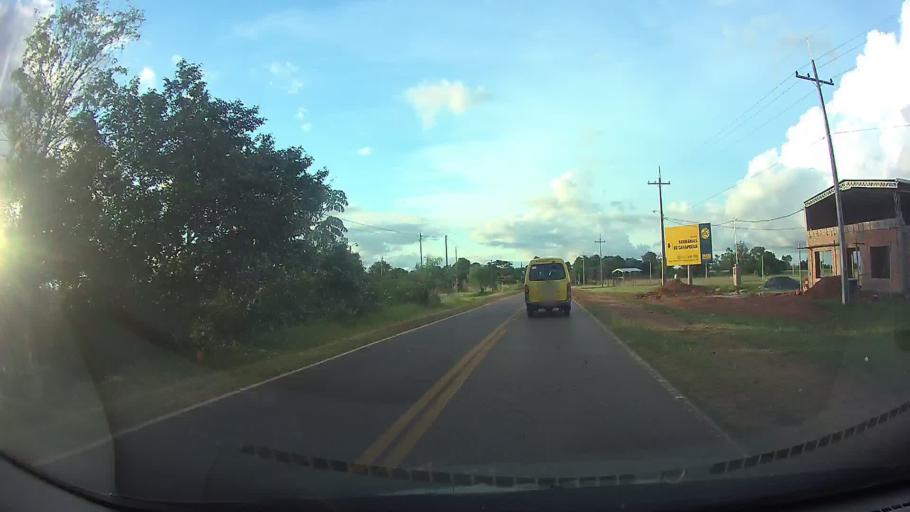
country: PY
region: Paraguari
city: Carapegua
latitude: -25.7841
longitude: -57.2208
